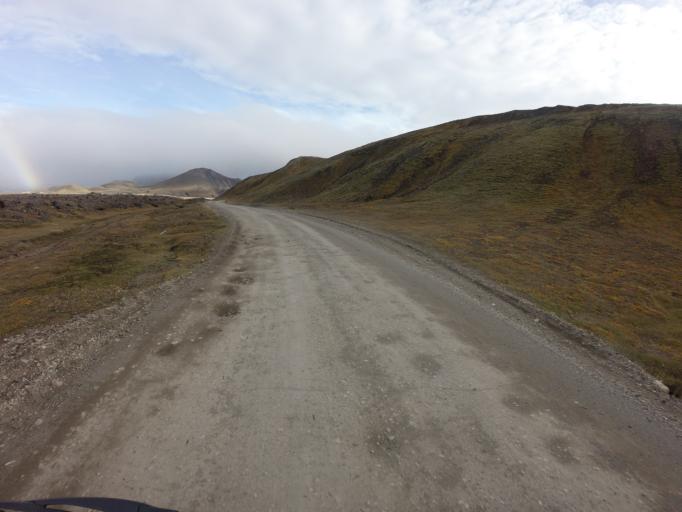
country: IS
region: South
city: Vestmannaeyjar
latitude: 64.0070
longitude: -19.0410
